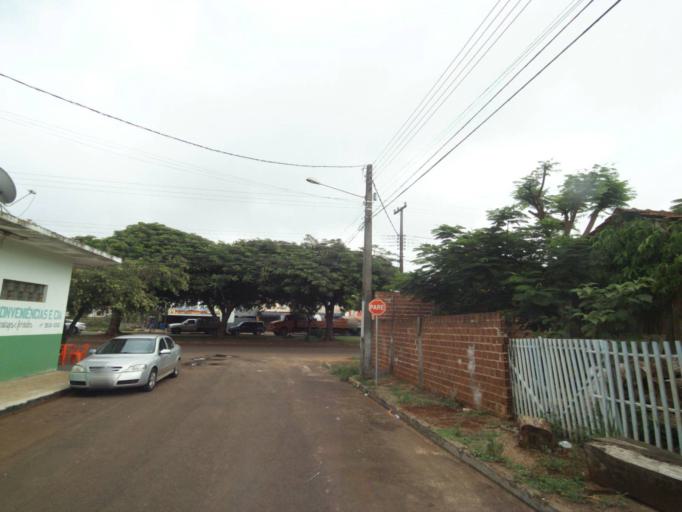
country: BR
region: Parana
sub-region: Campo Mourao
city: Campo Mourao
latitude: -24.0262
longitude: -52.3623
